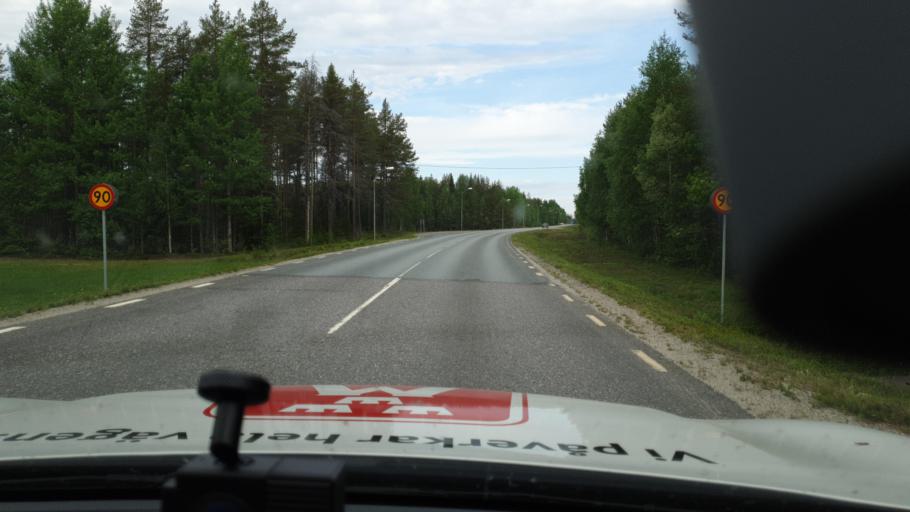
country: SE
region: Vaesterbotten
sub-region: Mala Kommun
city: Mala
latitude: 64.9908
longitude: 18.4943
